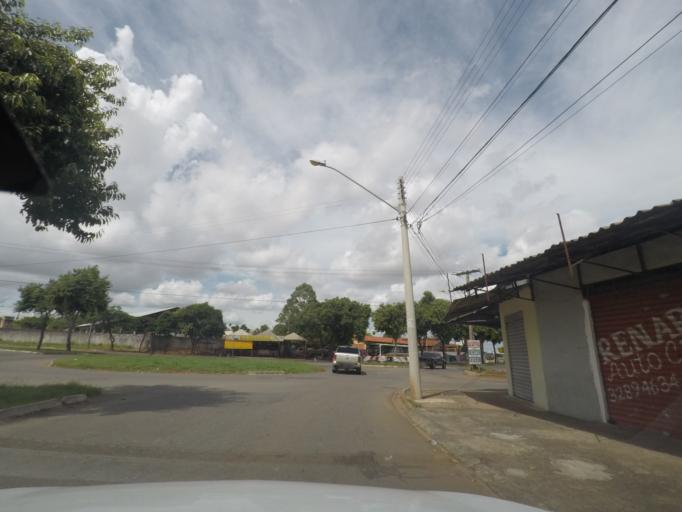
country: BR
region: Goias
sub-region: Goiania
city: Goiania
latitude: -16.7182
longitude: -49.3333
